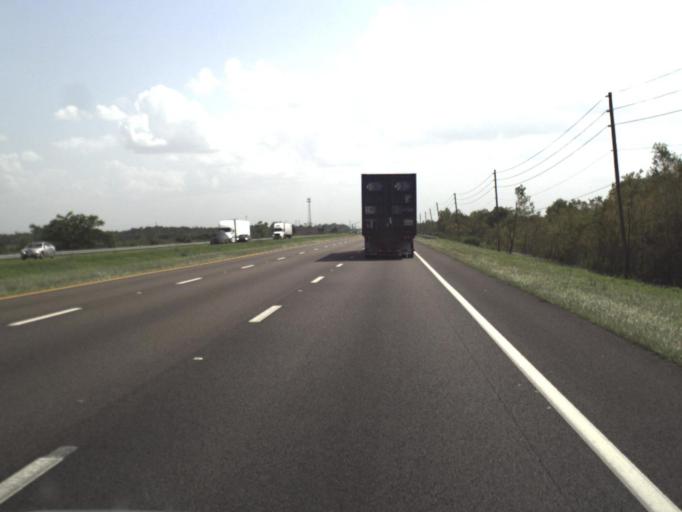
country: US
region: Florida
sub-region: Polk County
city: Dundee
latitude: 27.9892
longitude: -81.6313
